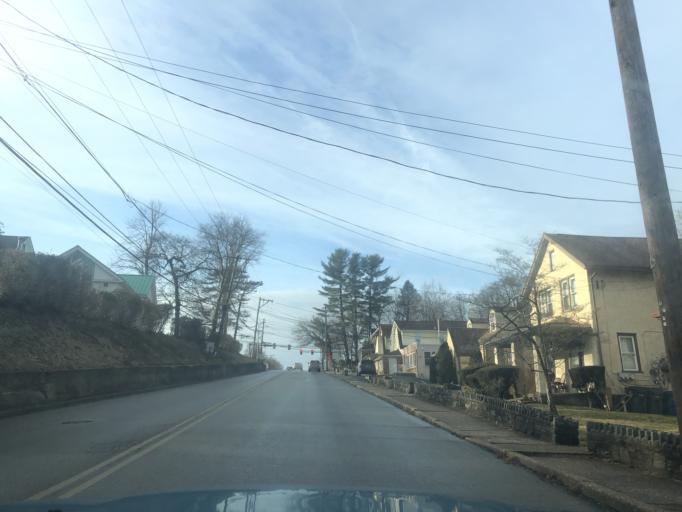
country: US
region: Pennsylvania
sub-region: Montgomery County
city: Glenside
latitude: 40.1190
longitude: -75.1355
